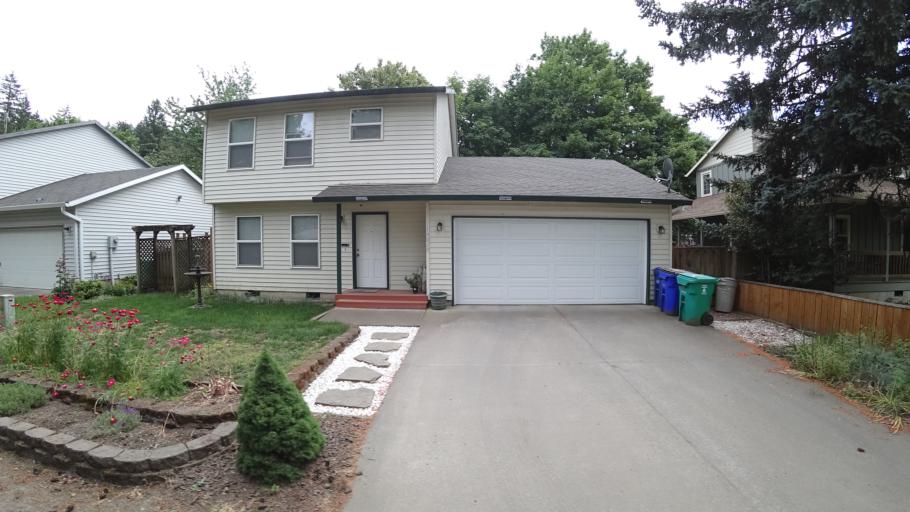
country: US
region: Oregon
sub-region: Clackamas County
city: Happy Valley
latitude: 45.4923
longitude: -122.5187
